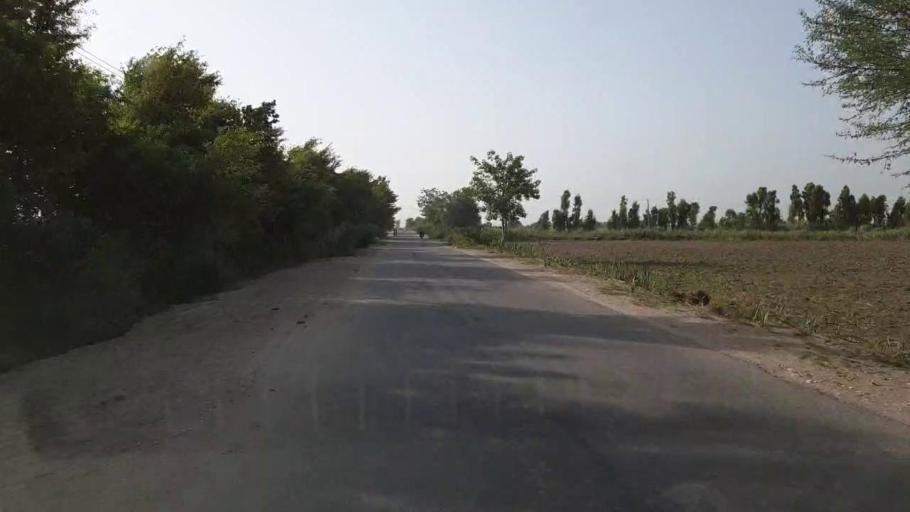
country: PK
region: Sindh
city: Jam Sahib
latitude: 26.3893
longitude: 68.8818
